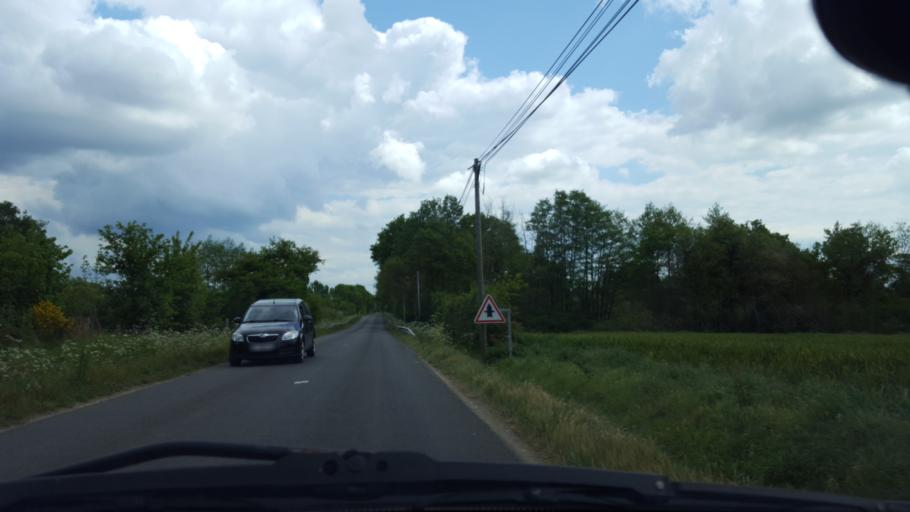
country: FR
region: Pays de la Loire
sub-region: Departement de la Loire-Atlantique
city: Saint-Philbert-de-Grand-Lieu
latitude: 47.0446
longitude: -1.6168
